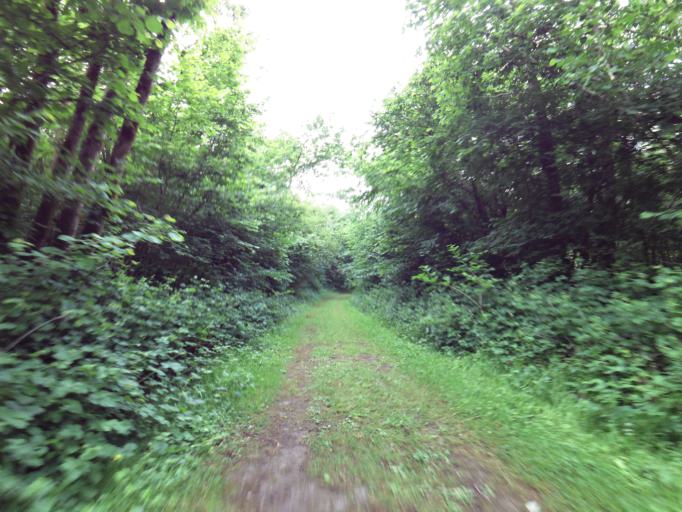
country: IE
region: Connaught
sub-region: County Galway
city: Gort
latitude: 53.0850
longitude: -8.8676
